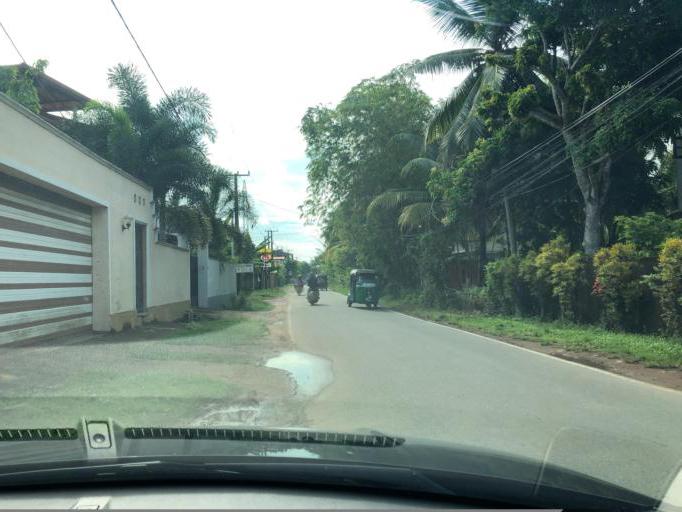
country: LK
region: Western
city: Kalutara
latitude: 6.5642
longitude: 79.9766
